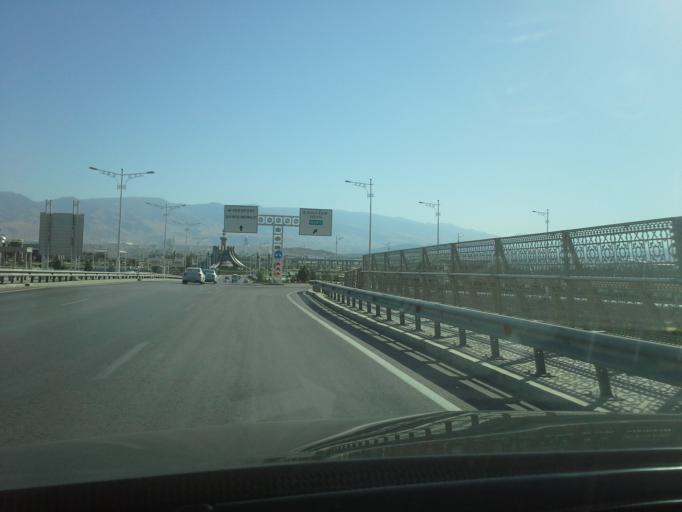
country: TM
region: Ahal
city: Ashgabat
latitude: 37.9769
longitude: 58.3943
